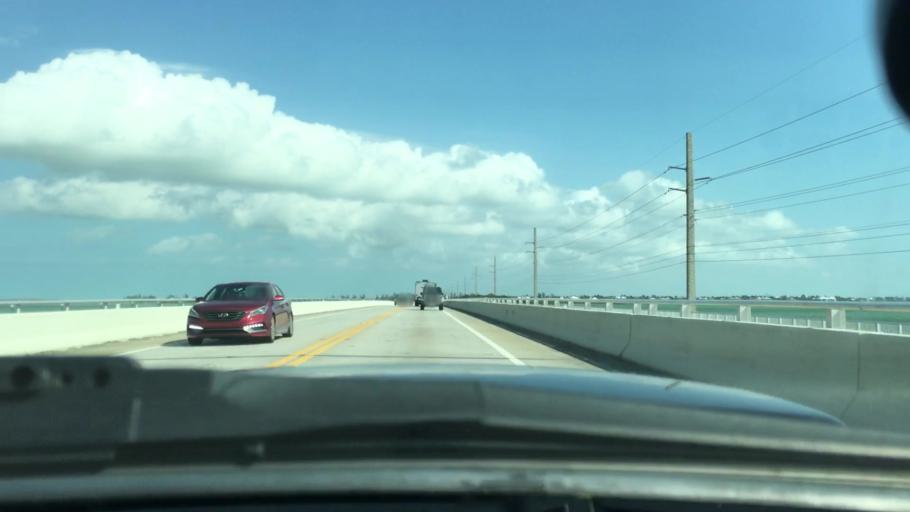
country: US
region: Florida
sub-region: Monroe County
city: Big Coppitt Key
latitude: 24.6327
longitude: -81.5871
